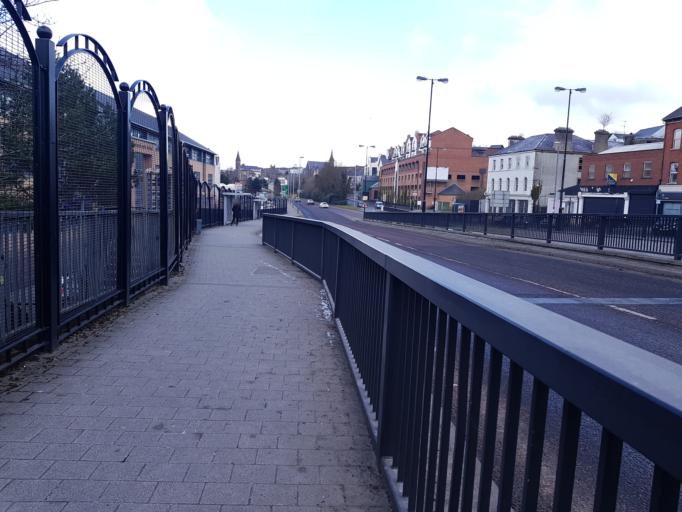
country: GB
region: Northern Ireland
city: Londonderry County Borough
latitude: 54.9900
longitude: -7.3152
